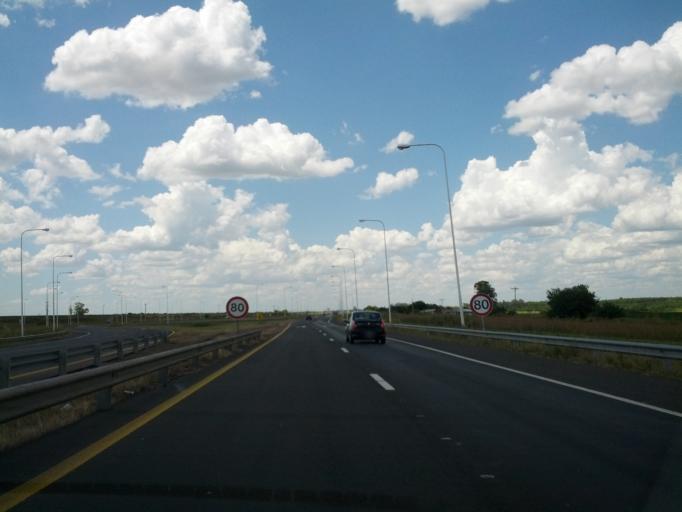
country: AR
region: Entre Rios
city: Colonia Elia
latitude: -32.5432
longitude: -58.3486
